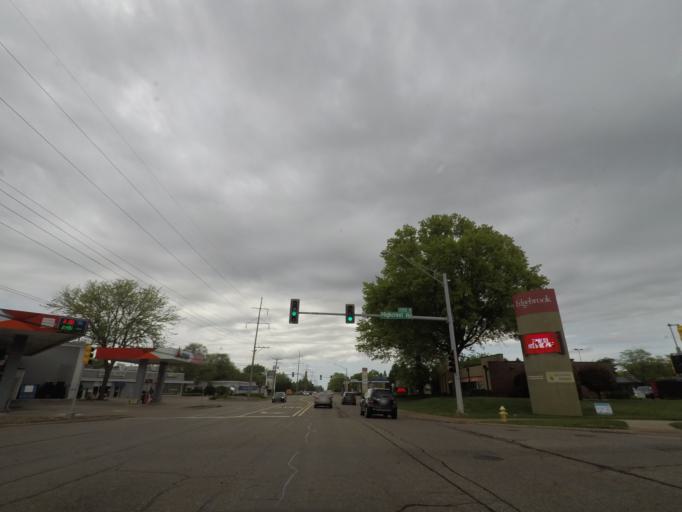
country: US
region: Illinois
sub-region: Winnebago County
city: Loves Park
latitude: 42.2854
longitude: -89.0290
